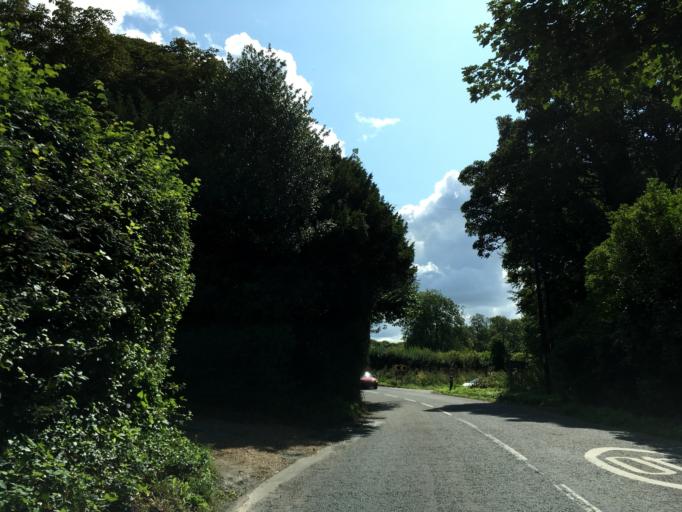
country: GB
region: England
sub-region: Hampshire
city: Colden Common
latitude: 51.0262
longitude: -1.2747
